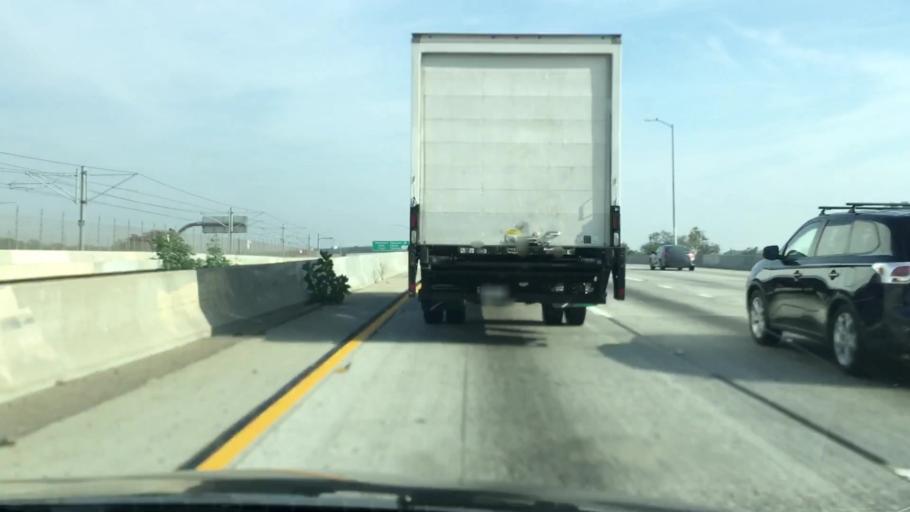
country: US
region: California
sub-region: Los Angeles County
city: Norwalk
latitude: 33.9137
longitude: -118.1118
